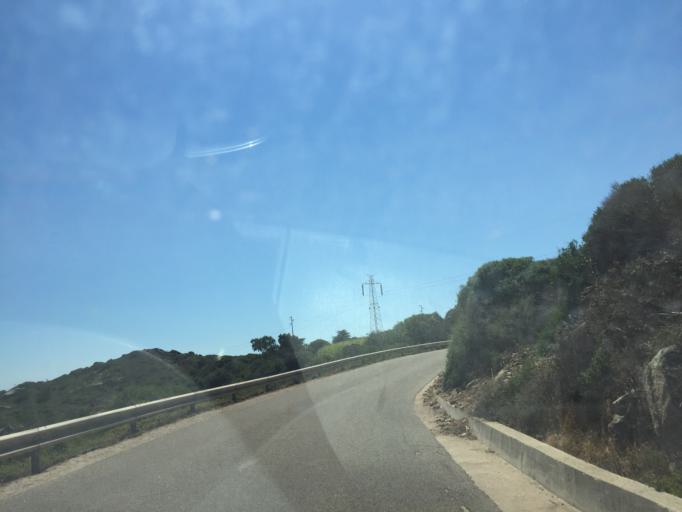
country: IT
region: Sardinia
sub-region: Provincia di Olbia-Tempio
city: Santa Teresa Gallura
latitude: 41.2383
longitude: 9.1797
